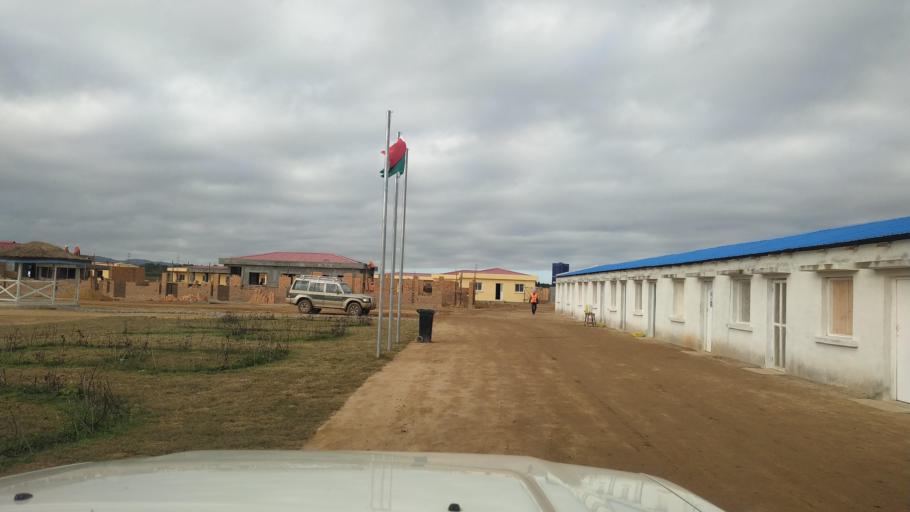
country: MG
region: Analamanga
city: Anjozorobe
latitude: -18.2748
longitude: 48.2625
